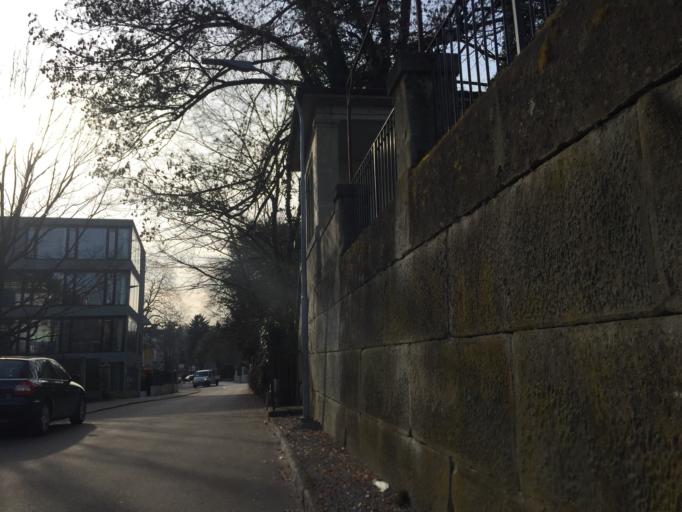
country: CH
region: Bern
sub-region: Bern-Mittelland District
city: Bern
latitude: 46.9468
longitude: 7.4302
